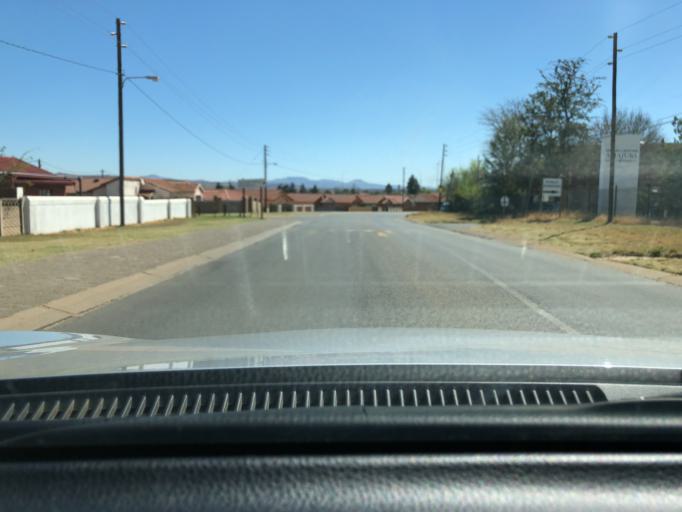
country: ZA
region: KwaZulu-Natal
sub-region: Amajuba District Municipality
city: Newcastle
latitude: -27.7612
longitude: 30.0246
